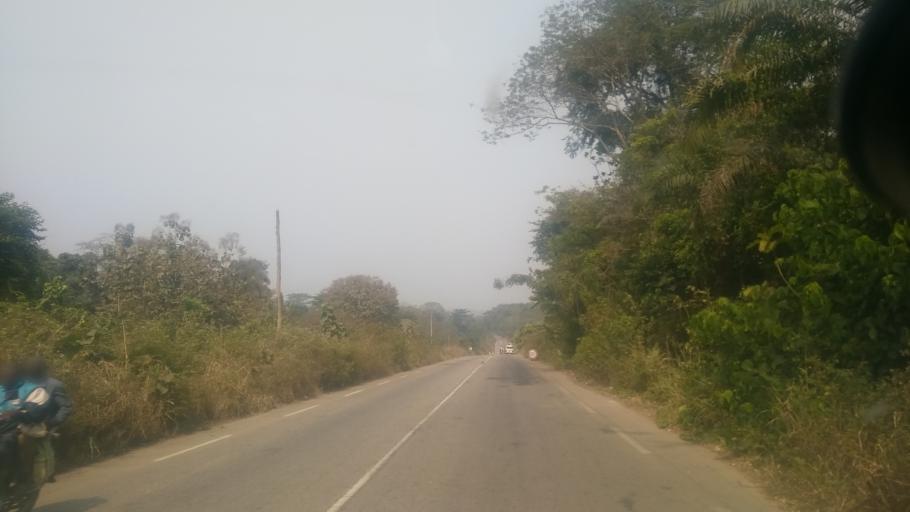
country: CM
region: Centre
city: Bafia
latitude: 4.7712
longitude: 11.2018
